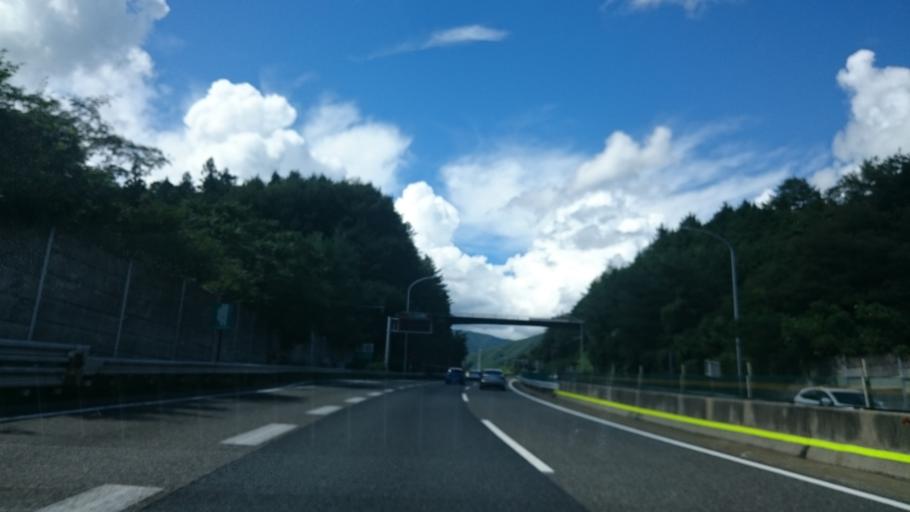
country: JP
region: Nagano
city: Iida
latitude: 35.4477
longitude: 137.7170
